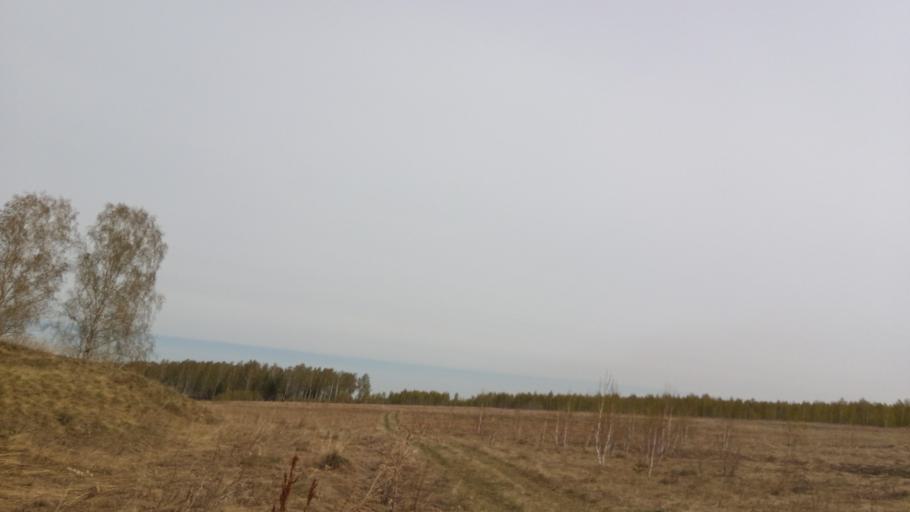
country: RU
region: Chelyabinsk
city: Timiryazevskiy
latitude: 55.0119
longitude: 60.8614
